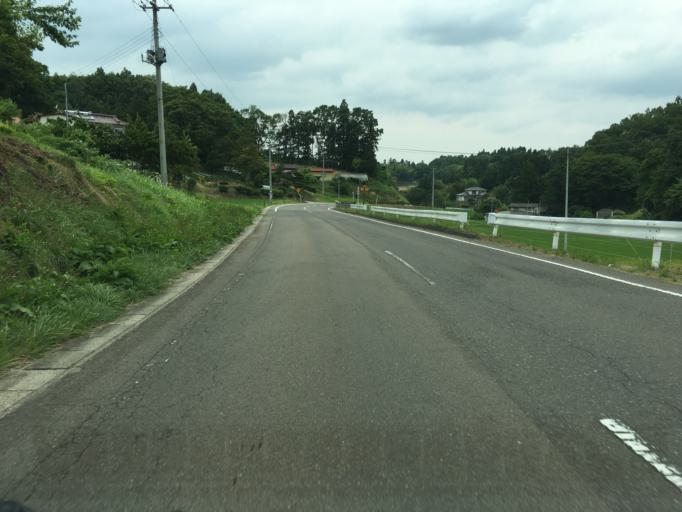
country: JP
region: Fukushima
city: Nihommatsu
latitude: 37.6334
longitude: 140.5392
